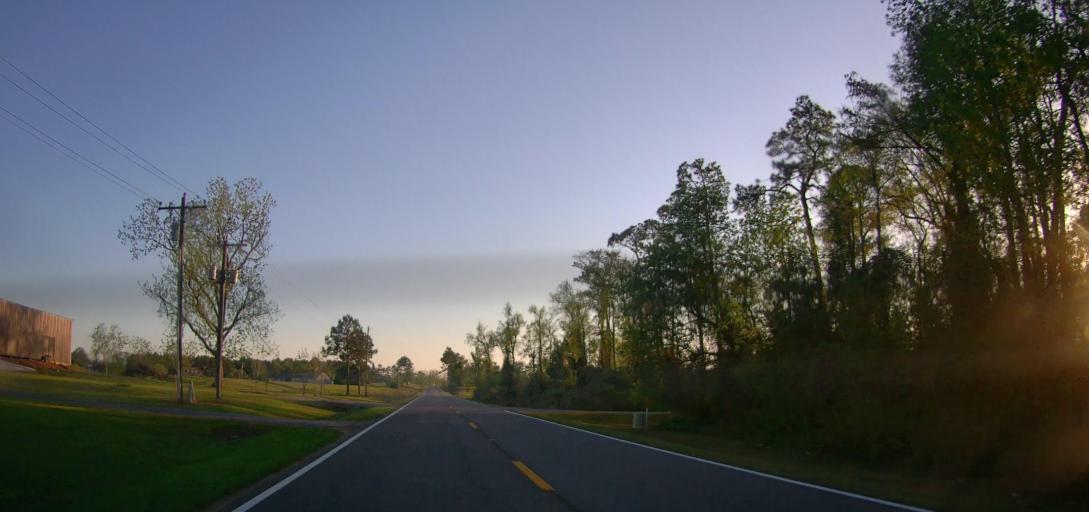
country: US
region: Georgia
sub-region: Irwin County
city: Ocilla
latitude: 31.6467
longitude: -83.2676
